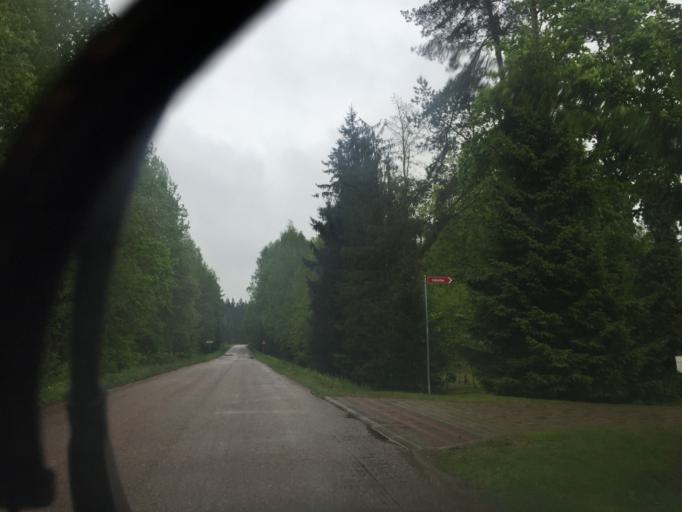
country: LV
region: Ogre
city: Jumprava
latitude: 56.6783
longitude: 24.9793
